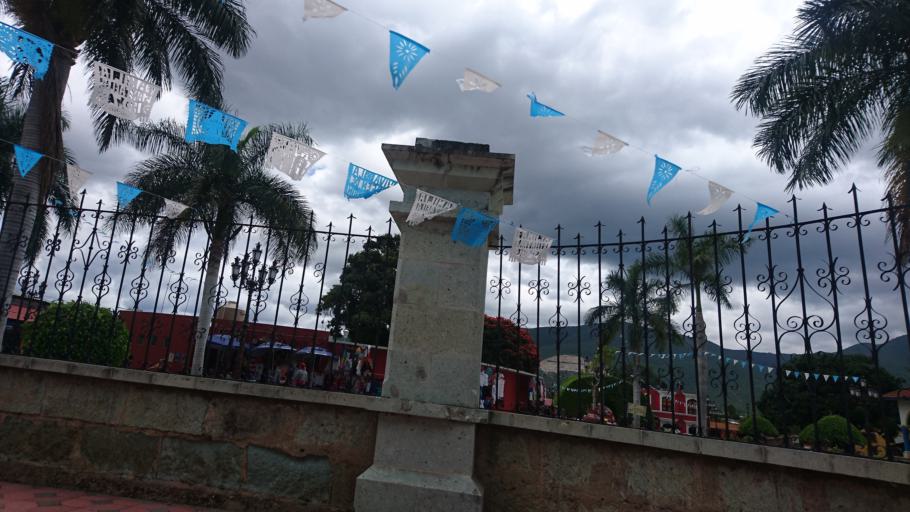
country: MX
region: Oaxaca
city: Santa Maria del Tule
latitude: 17.0462
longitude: -96.6364
